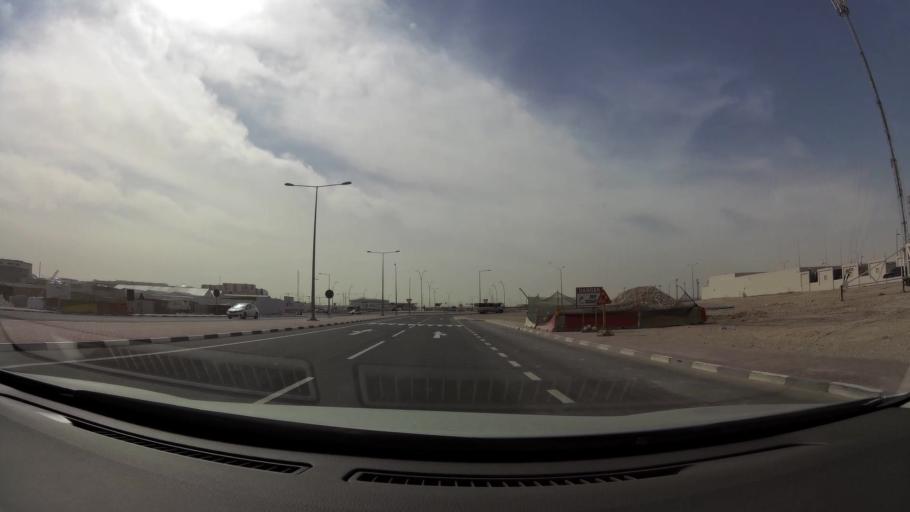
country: QA
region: Baladiyat ar Rayyan
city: Ar Rayyan
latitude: 25.3298
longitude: 51.3565
